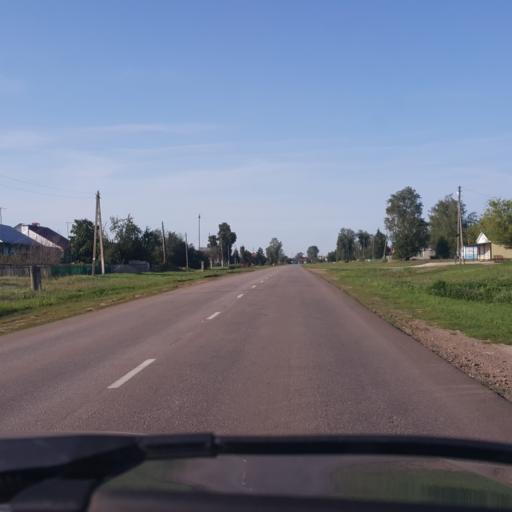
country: RU
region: Tambov
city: Novaya Lyada
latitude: 52.7803
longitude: 41.7605
